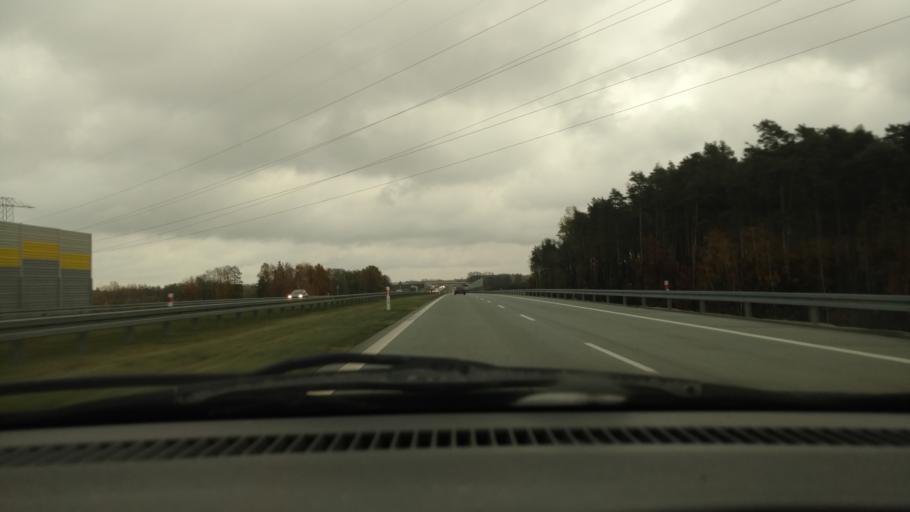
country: PL
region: Lodz Voivodeship
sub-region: Powiat pabianicki
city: Pabianice
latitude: 51.6078
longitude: 19.3236
